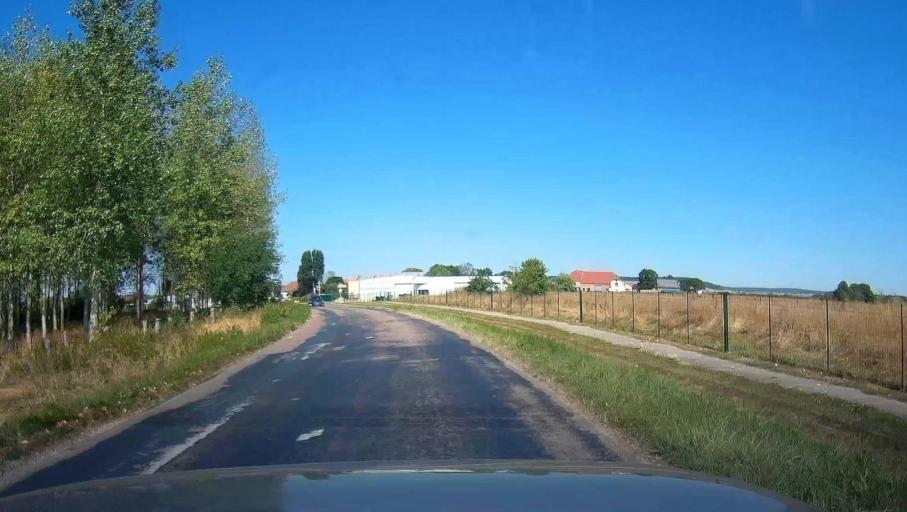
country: FR
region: Champagne-Ardenne
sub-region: Departement de la Haute-Marne
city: Langres
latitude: 47.8789
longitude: 5.3697
